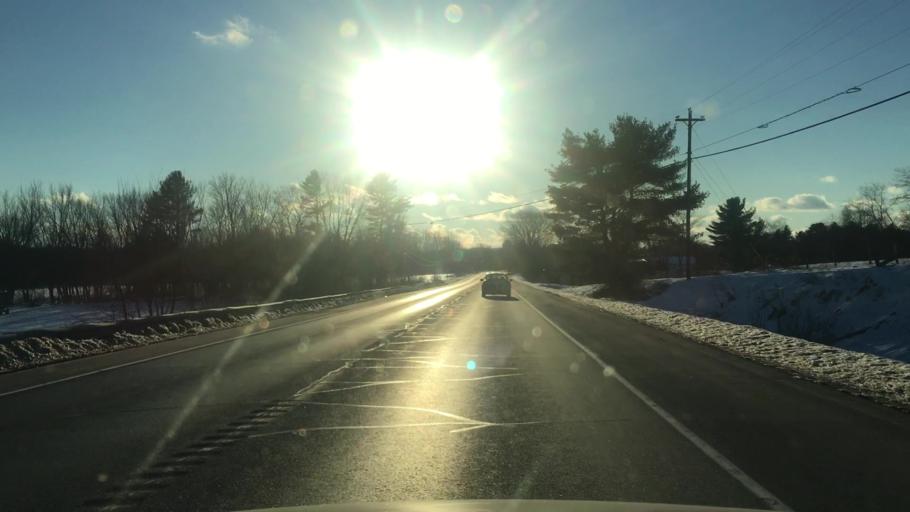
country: US
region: Maine
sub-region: Franklin County
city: New Sharon
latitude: 44.6420
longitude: -70.0374
